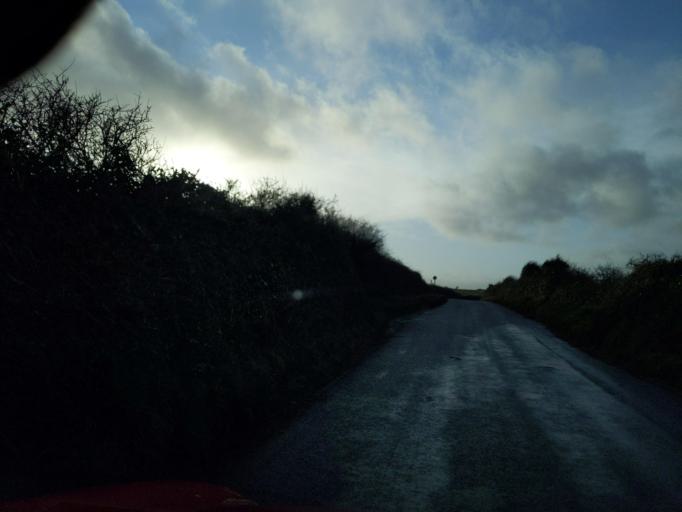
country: GB
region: England
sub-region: Cornwall
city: Fowey
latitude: 50.3298
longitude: -4.6164
